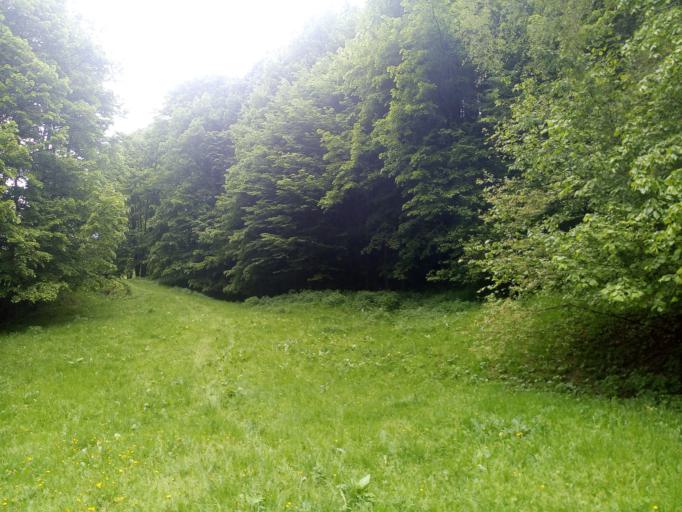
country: PL
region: Lesser Poland Voivodeship
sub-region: Powiat nowotarski
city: Szczawnica
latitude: 49.4961
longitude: 20.4870
